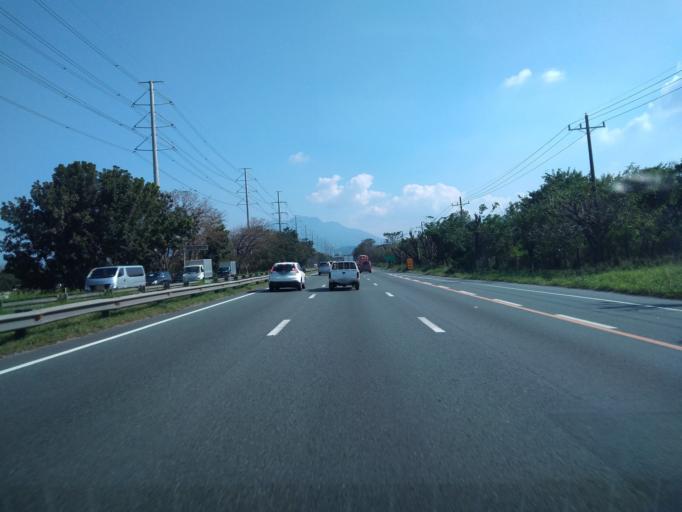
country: PH
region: Calabarzon
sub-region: Province of Laguna
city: Prinza
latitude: 14.2281
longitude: 121.1196
